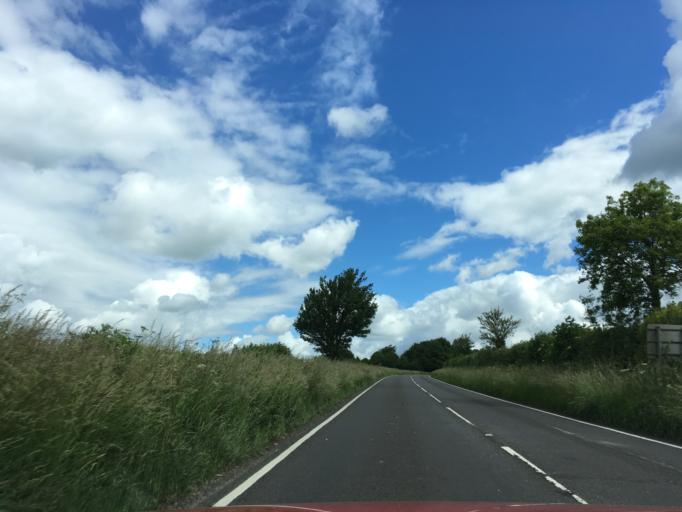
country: GB
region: England
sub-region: Oxfordshire
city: Shipton under Wychwood
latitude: 51.8670
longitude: -1.5889
